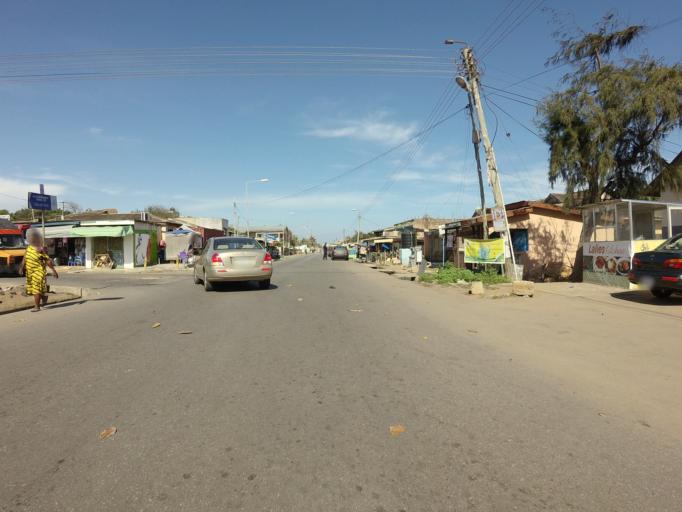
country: GH
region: Greater Accra
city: Accra
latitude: 5.5615
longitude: -0.1526
